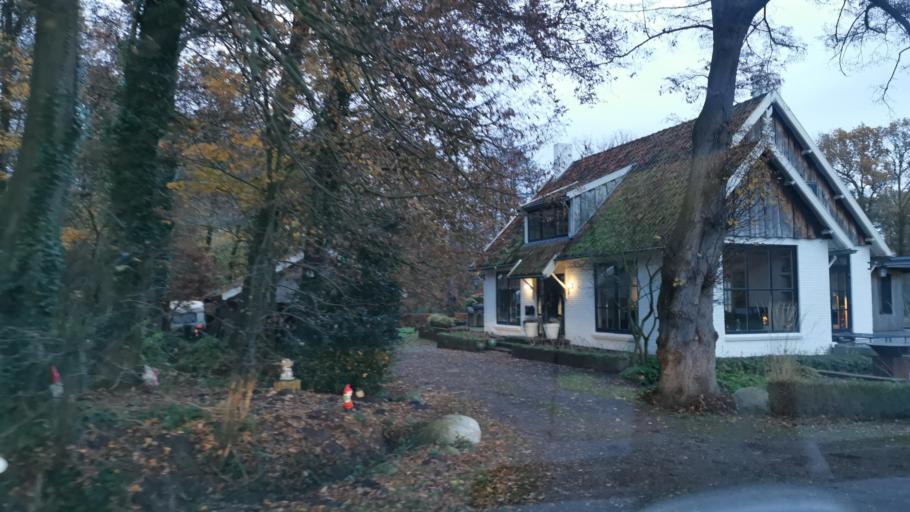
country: NL
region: Overijssel
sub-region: Gemeente Oldenzaal
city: Oldenzaal
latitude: 52.3133
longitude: 6.9564
